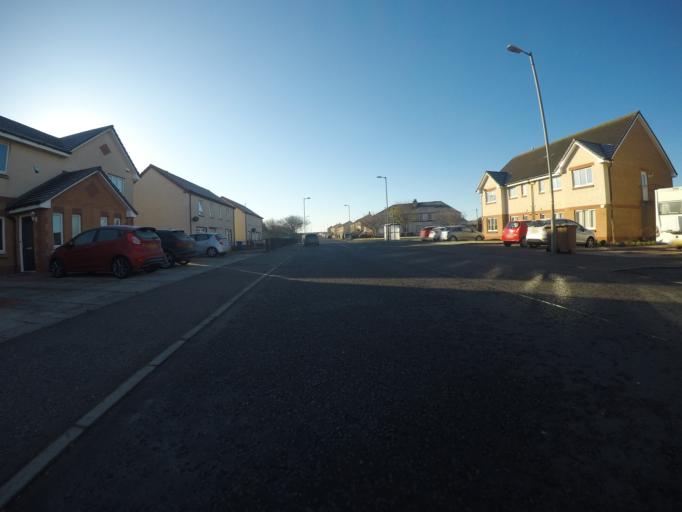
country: GB
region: Scotland
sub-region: North Ayrshire
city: Stevenston
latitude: 55.6329
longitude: -4.7430
